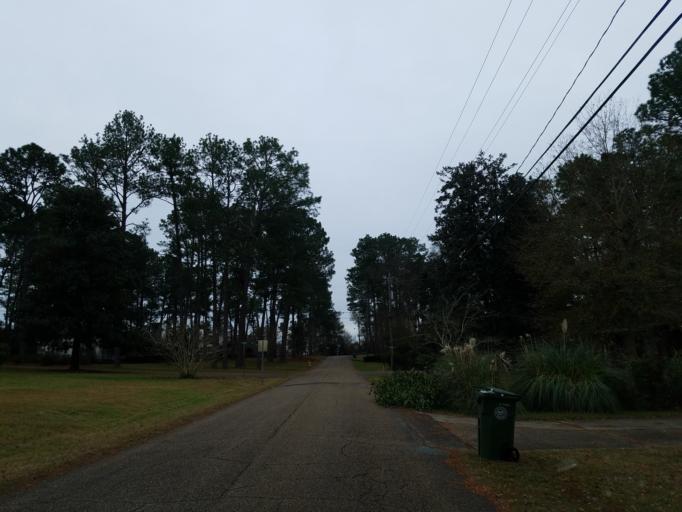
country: US
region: Mississippi
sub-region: Forrest County
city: Hattiesburg
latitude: 31.3151
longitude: -89.3185
